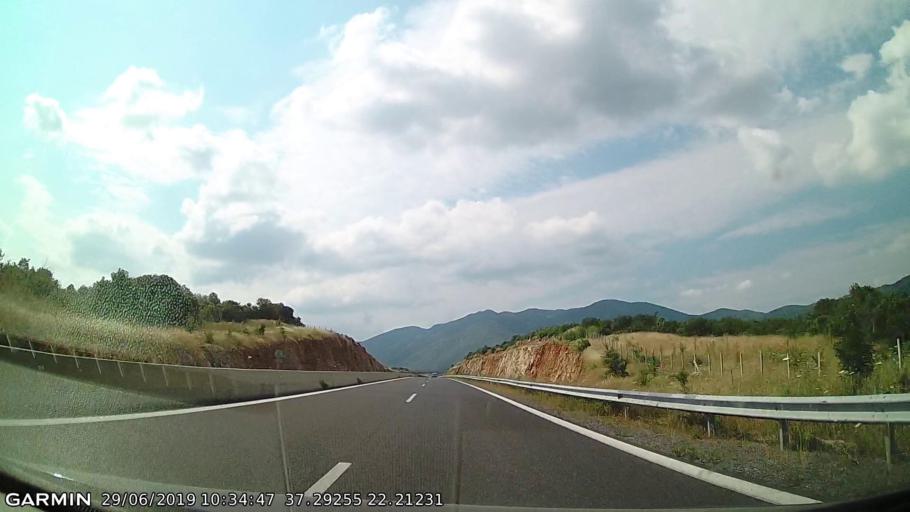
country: GR
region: Peloponnese
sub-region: Nomos Arkadias
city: Megalopoli
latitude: 37.2925
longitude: 22.2125
